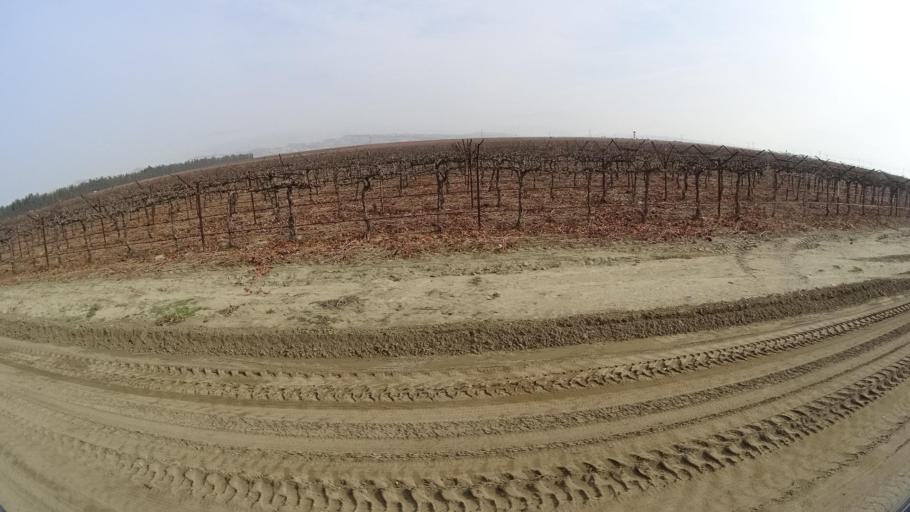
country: US
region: California
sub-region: Kern County
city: Arvin
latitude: 35.0966
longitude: -118.8505
